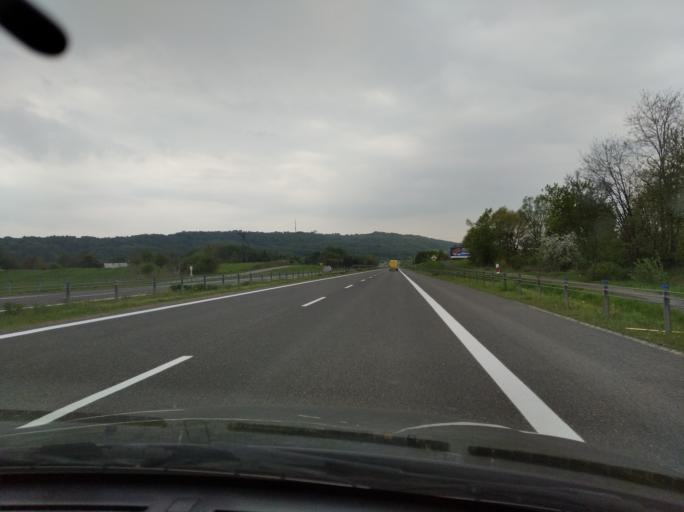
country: PL
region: Lesser Poland Voivodeship
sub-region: Powiat tarnowski
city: Skrzyszow
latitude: 50.0040
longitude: 21.0424
